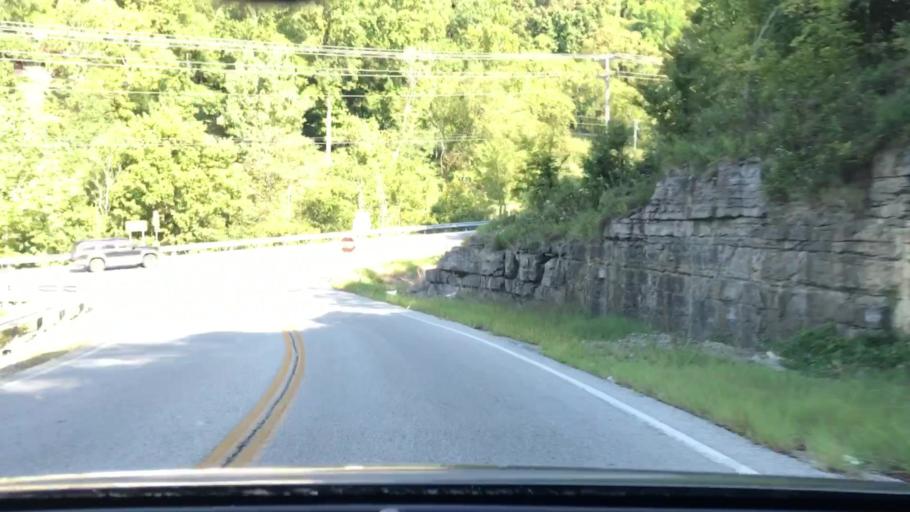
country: US
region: Tennessee
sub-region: Smith County
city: Carthage
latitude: 36.3211
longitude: -85.9420
